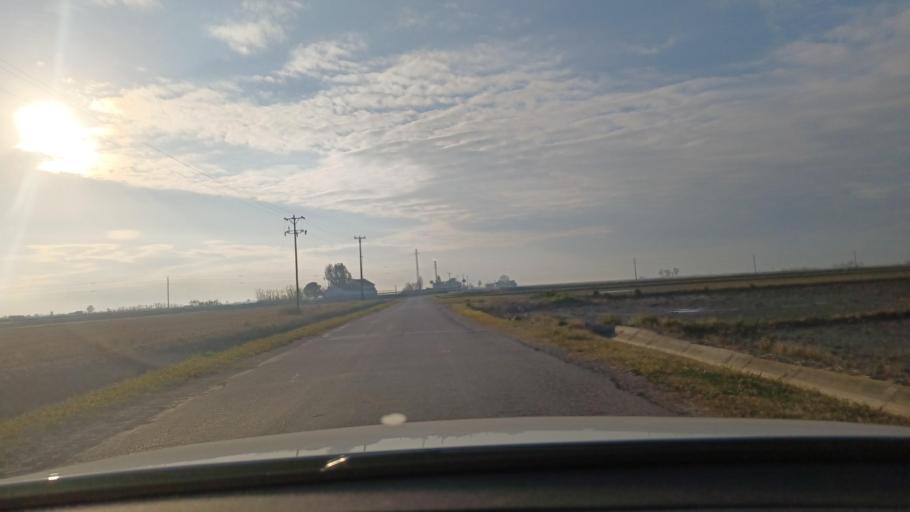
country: ES
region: Catalonia
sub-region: Provincia de Tarragona
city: Deltebre
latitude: 40.6778
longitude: 0.6594
